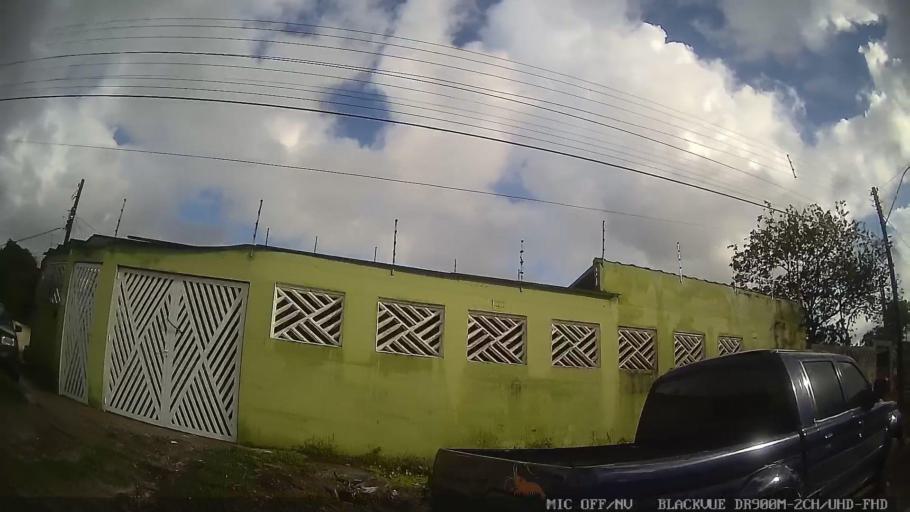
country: BR
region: Sao Paulo
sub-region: Itanhaem
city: Itanhaem
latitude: -24.1740
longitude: -46.8492
